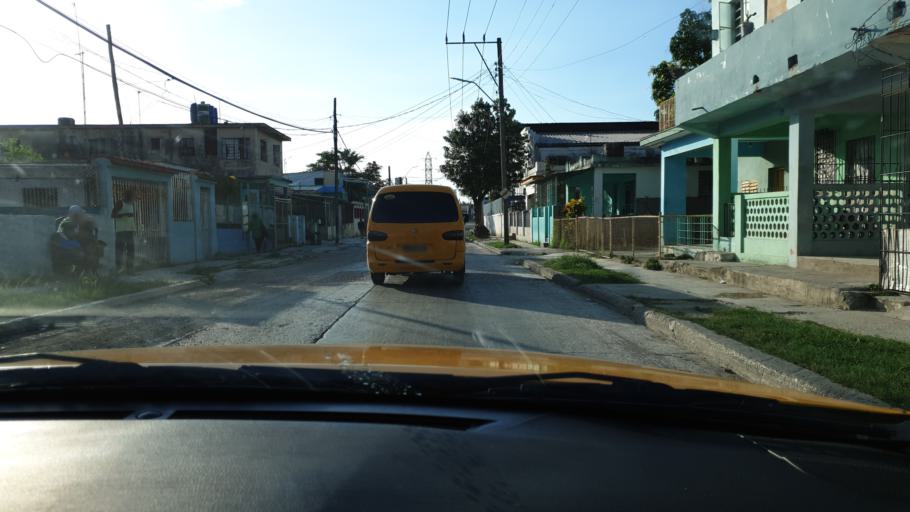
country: CU
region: La Habana
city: Regla
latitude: 23.1084
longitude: -82.3301
